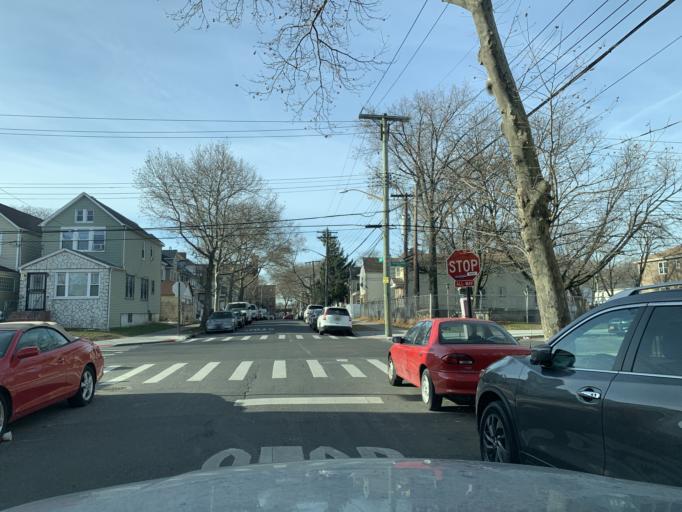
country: US
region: New York
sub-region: Queens County
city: Jamaica
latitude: 40.6963
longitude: -73.7919
